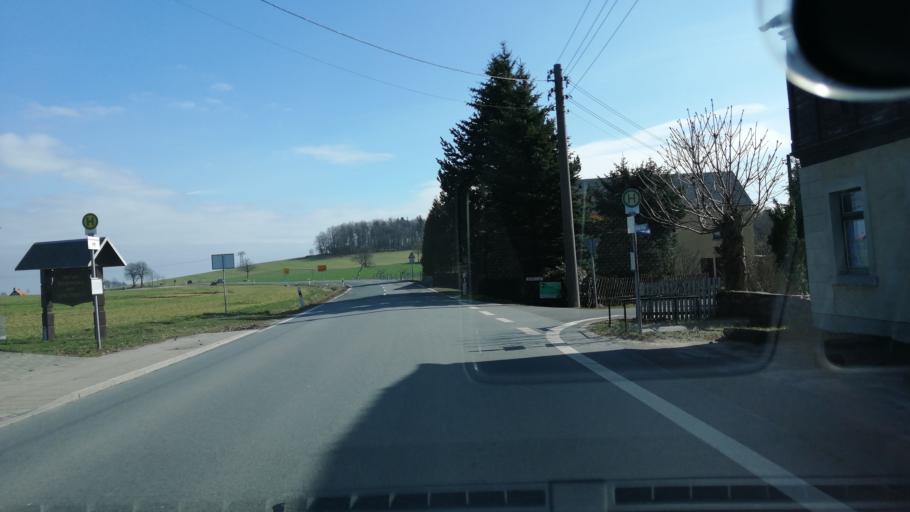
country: DE
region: Saxony
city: Schonbach
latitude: 51.0785
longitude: 14.5530
